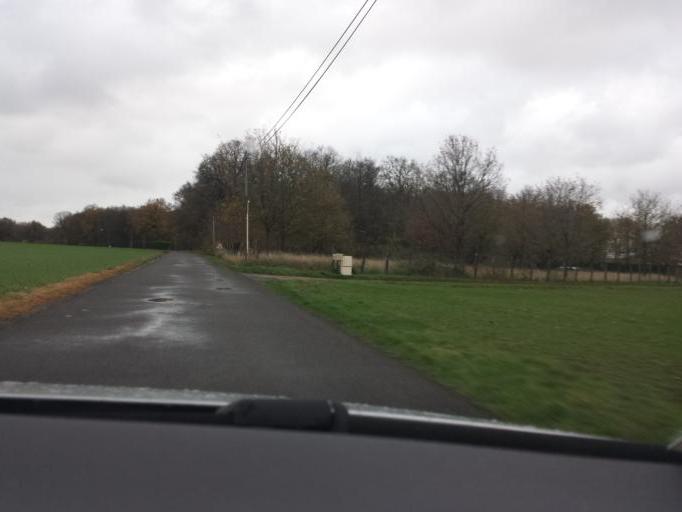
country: FR
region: Haute-Normandie
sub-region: Departement de l'Eure
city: Evreux
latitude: 49.0004
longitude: 1.2156
